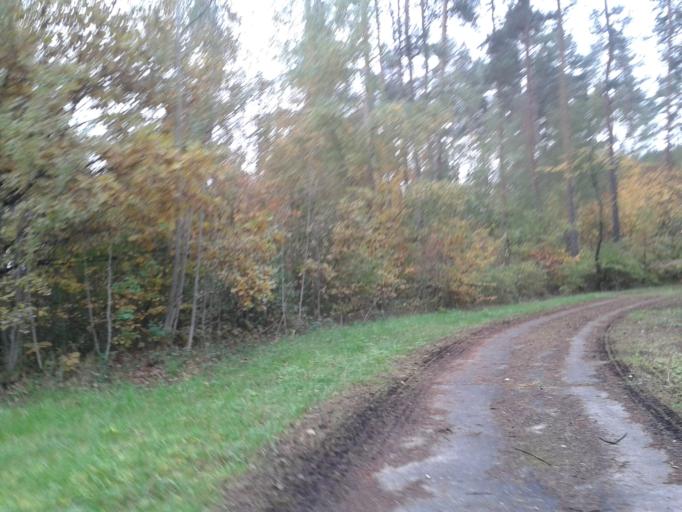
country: DE
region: Bavaria
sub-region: Upper Franconia
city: Gundelsheim
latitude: 49.9221
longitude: 10.9262
